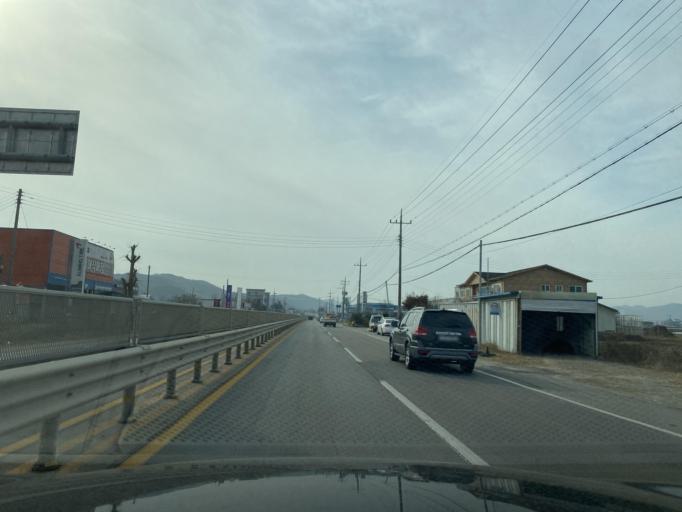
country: KR
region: Chungcheongnam-do
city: Yesan
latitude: 36.6880
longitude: 126.8273
